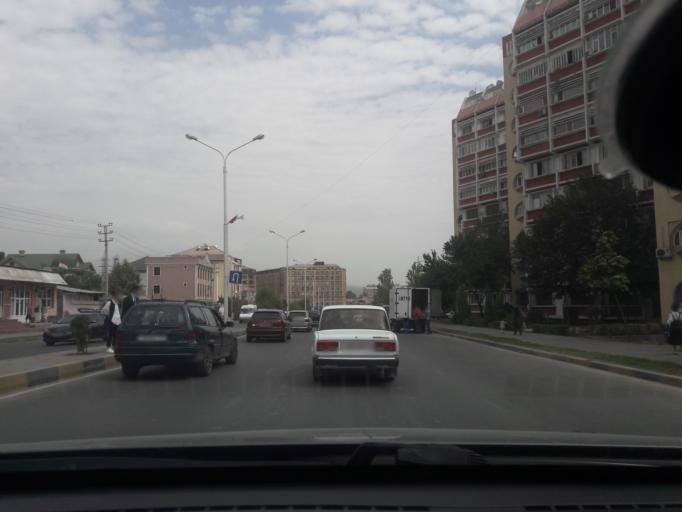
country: TJ
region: Dushanbe
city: Dushanbe
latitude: 38.5911
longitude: 68.7370
